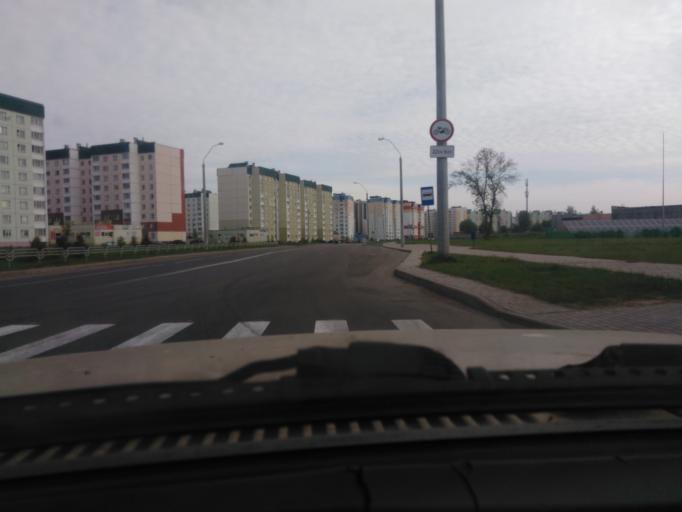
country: BY
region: Mogilev
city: Buynichy
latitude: 53.9114
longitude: 30.2840
